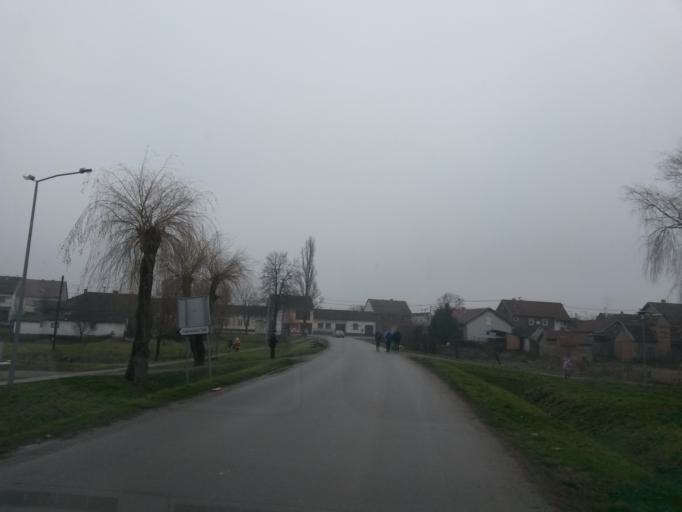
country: HR
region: Vukovarsko-Srijemska
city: Bosnjaci
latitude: 45.0520
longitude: 18.7494
